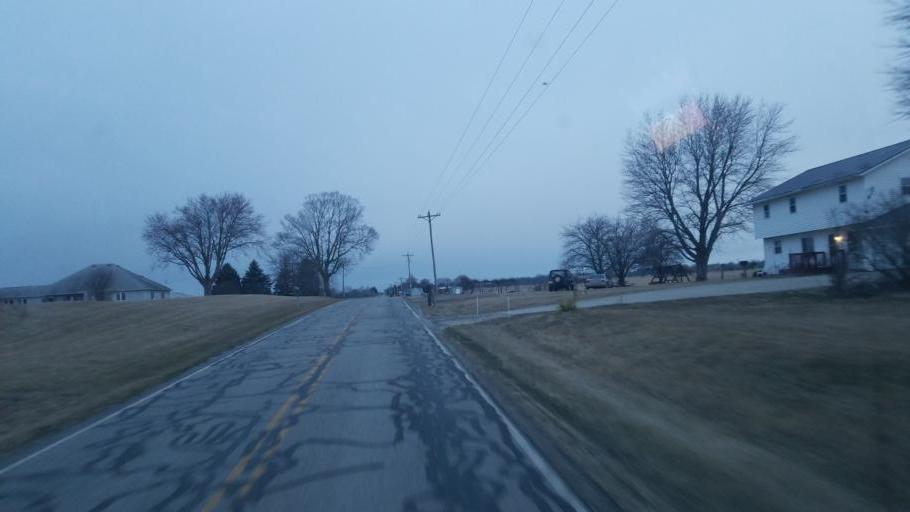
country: US
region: Ohio
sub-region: Defiance County
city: Hicksville
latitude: 41.3250
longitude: -84.7411
